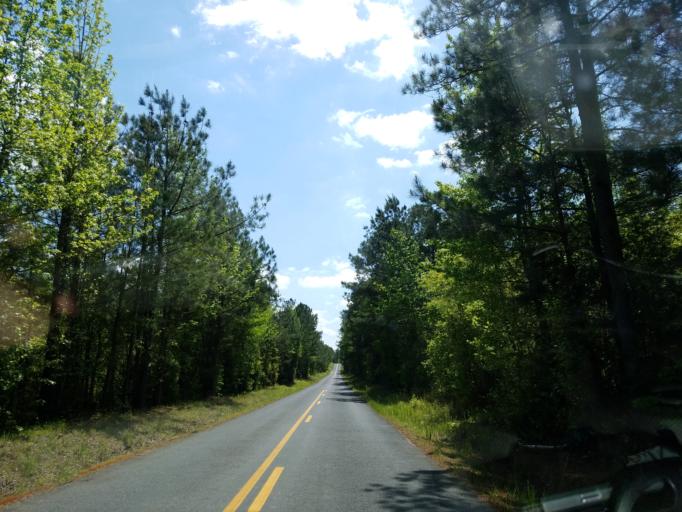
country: US
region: Georgia
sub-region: Butts County
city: Indian Springs
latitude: 33.1510
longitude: -84.0046
